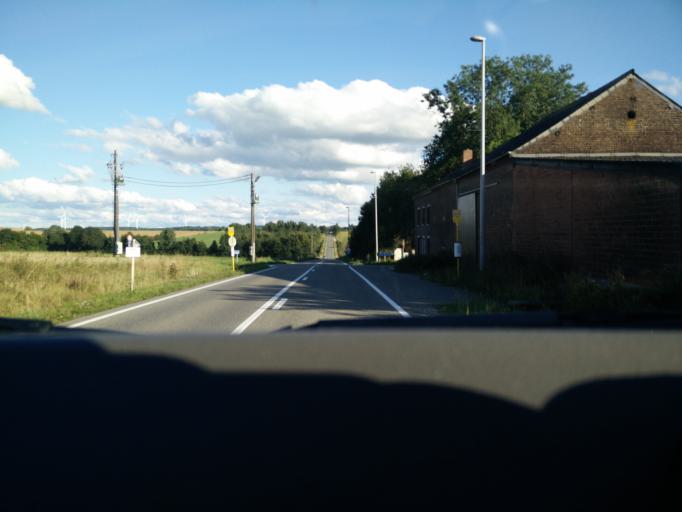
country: BE
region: Wallonia
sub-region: Province du Hainaut
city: Beaumont
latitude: 50.2312
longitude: 4.2694
